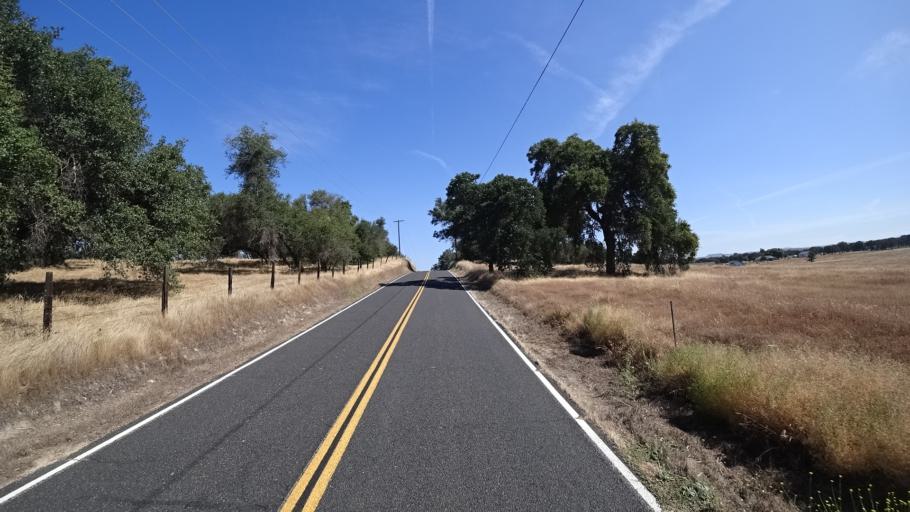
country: US
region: California
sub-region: Calaveras County
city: Rancho Calaveras
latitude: 38.1283
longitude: -120.9265
